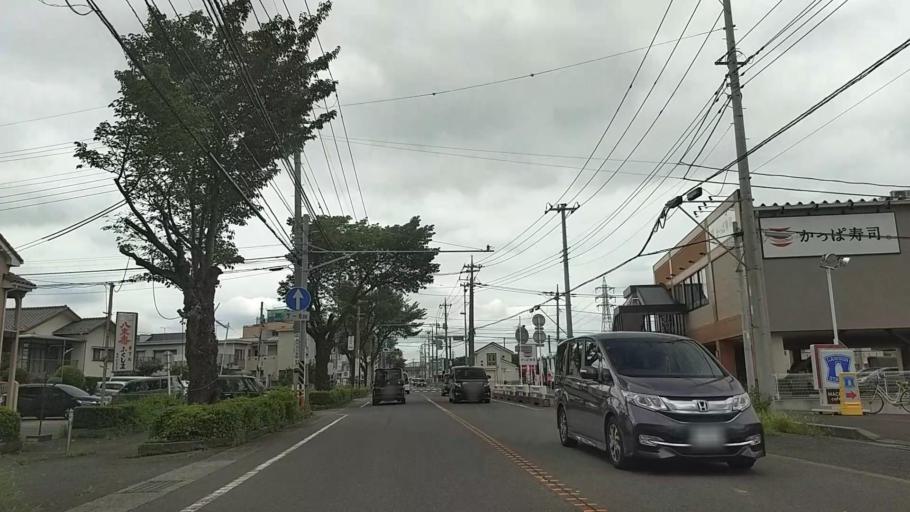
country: JP
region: Kanagawa
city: Minami-rinkan
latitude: 35.4253
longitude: 139.4684
